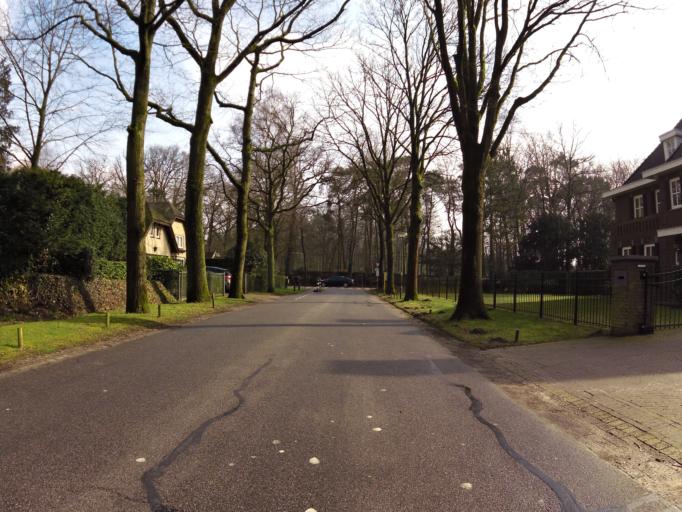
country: NL
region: North Brabant
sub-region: Gemeente Sint-Michielsgestel
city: Sint-Michielsgestel
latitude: 51.6324
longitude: 5.3396
